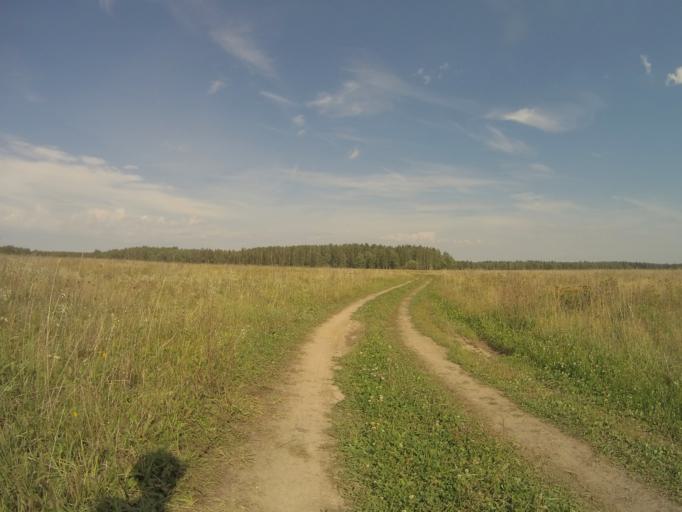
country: RU
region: Vladimir
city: Bogolyubovo
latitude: 56.1150
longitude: 40.5349
